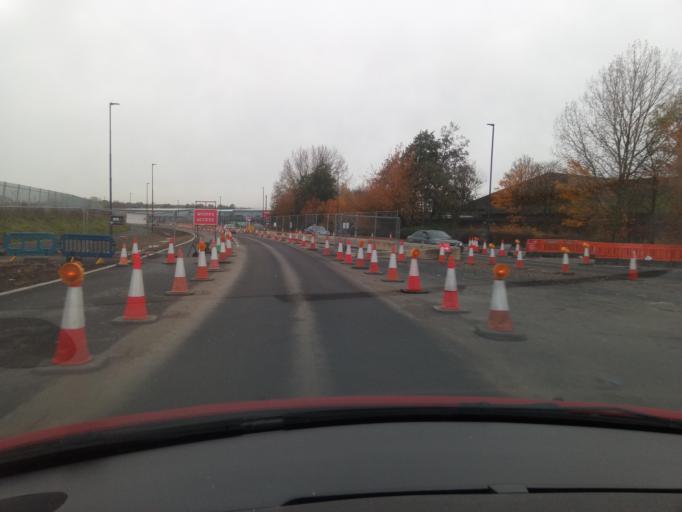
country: GB
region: England
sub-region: Derby
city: Derby
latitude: 52.9150
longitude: -1.4338
